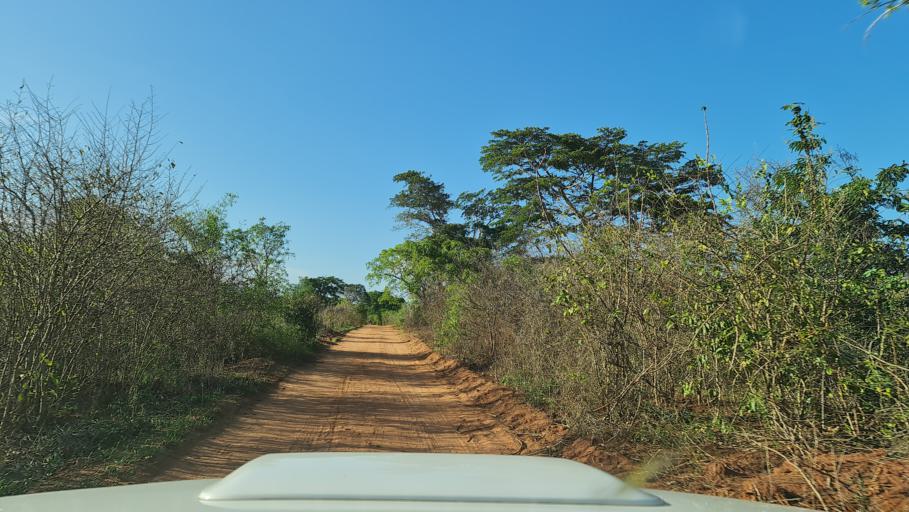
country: MZ
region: Nampula
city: Nacala
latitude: -14.7073
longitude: 40.3335
